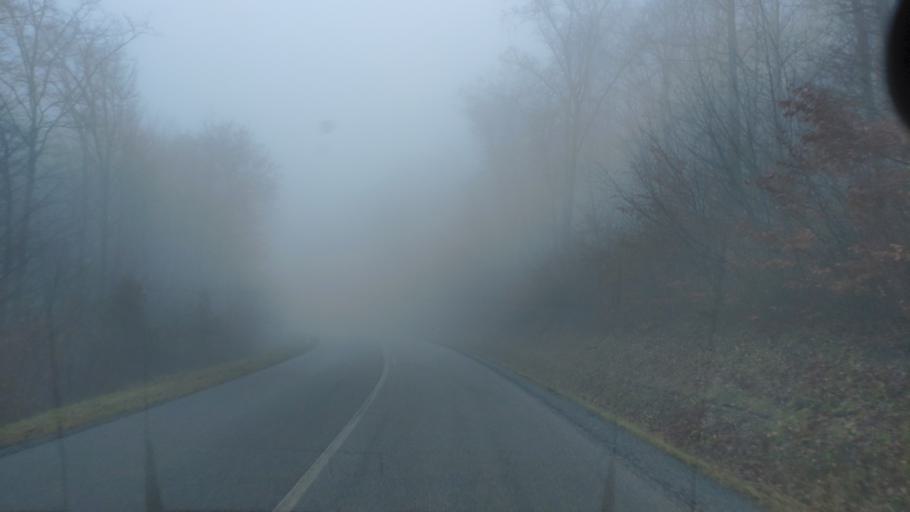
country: SK
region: Banskobystricky
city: Revuca
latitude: 48.6287
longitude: 20.2869
